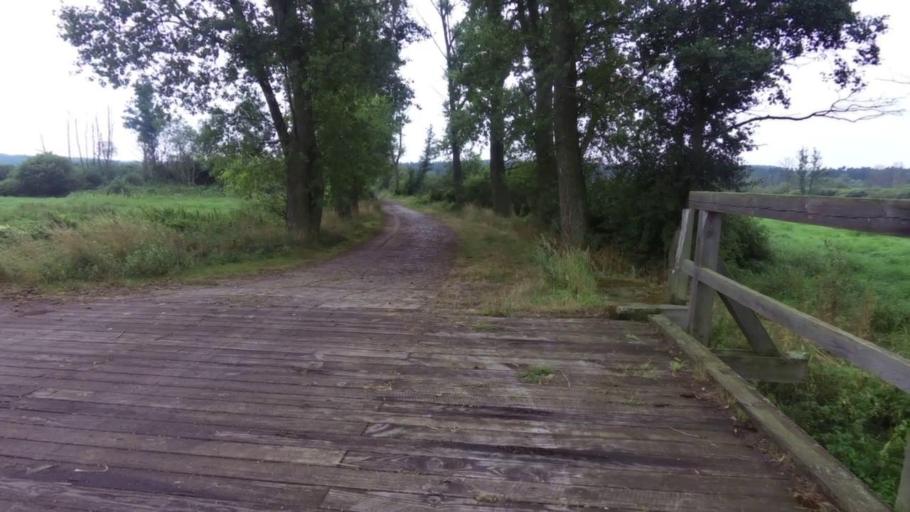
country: PL
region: West Pomeranian Voivodeship
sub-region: Powiat stargardzki
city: Suchan
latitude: 53.2502
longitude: 15.3842
